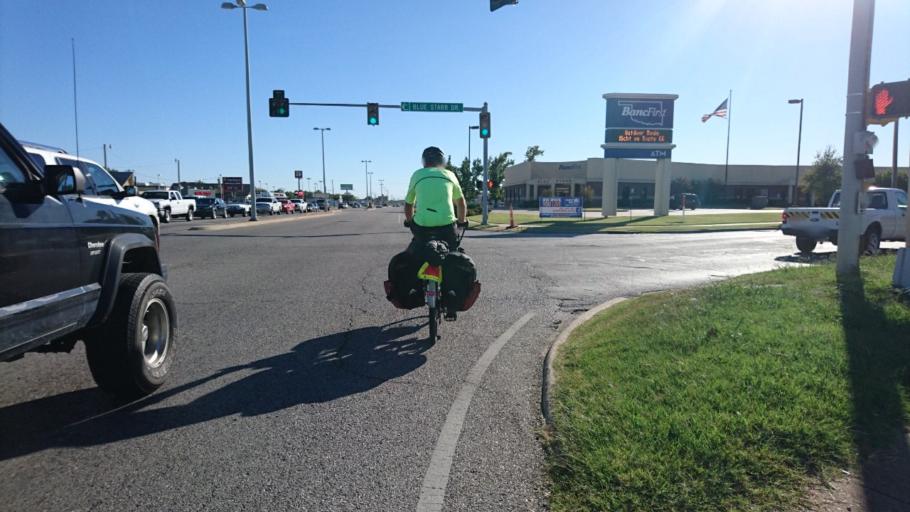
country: US
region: Oklahoma
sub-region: Rogers County
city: Claremore
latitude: 36.3219
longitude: -95.6104
